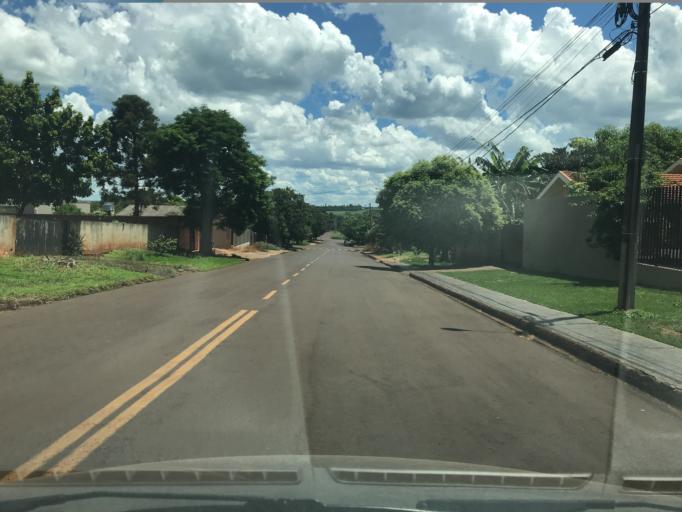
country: BR
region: Parana
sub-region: Palotina
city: Palotina
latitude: -24.2802
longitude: -53.8459
